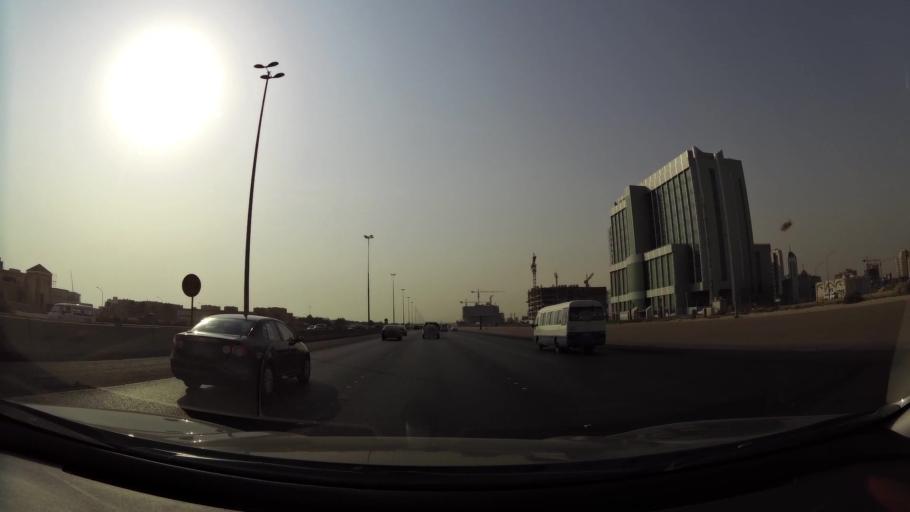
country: KW
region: Mubarak al Kabir
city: Sabah as Salim
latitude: 29.2596
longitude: 48.0879
